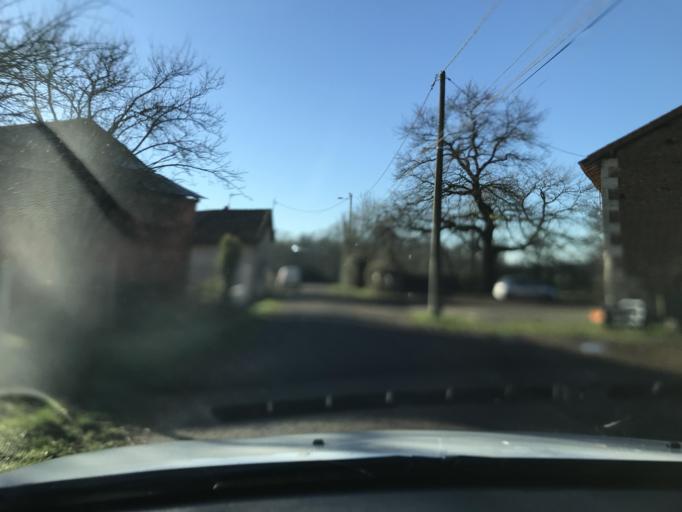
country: FR
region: Poitou-Charentes
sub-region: Departement de la Charente
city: Loubert
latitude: 45.8469
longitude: 0.5438
